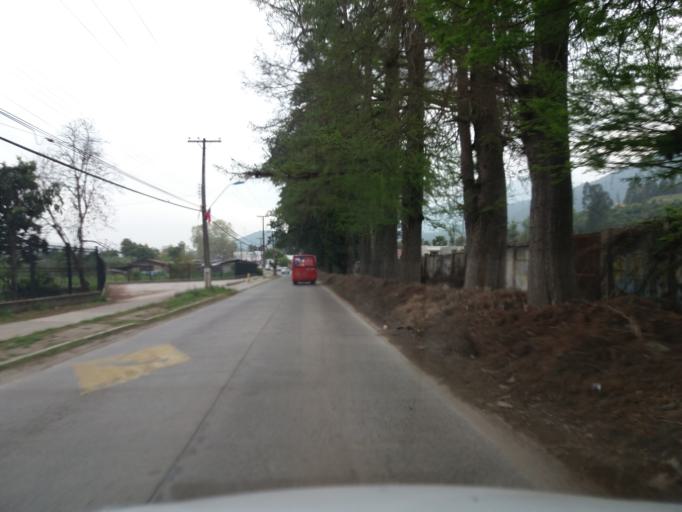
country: CL
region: Valparaiso
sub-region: Provincia de Quillota
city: Hacienda La Calera
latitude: -32.8046
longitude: -71.1431
